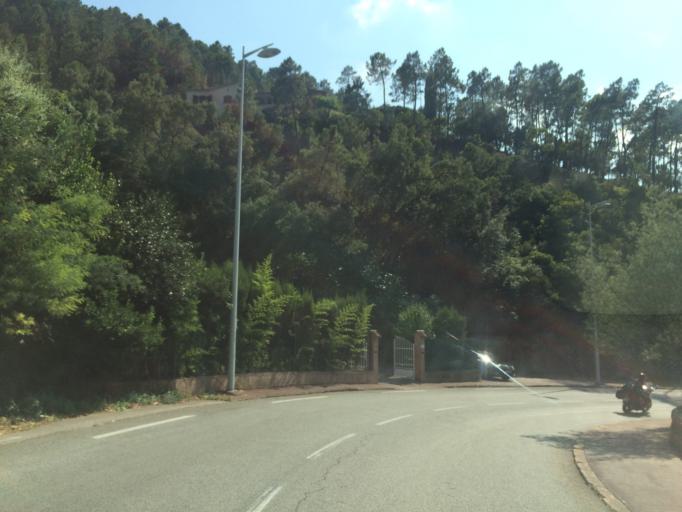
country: FR
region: Provence-Alpes-Cote d'Azur
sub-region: Departement des Alpes-Maritimes
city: Theoule-sur-Mer
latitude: 43.5060
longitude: 6.9421
